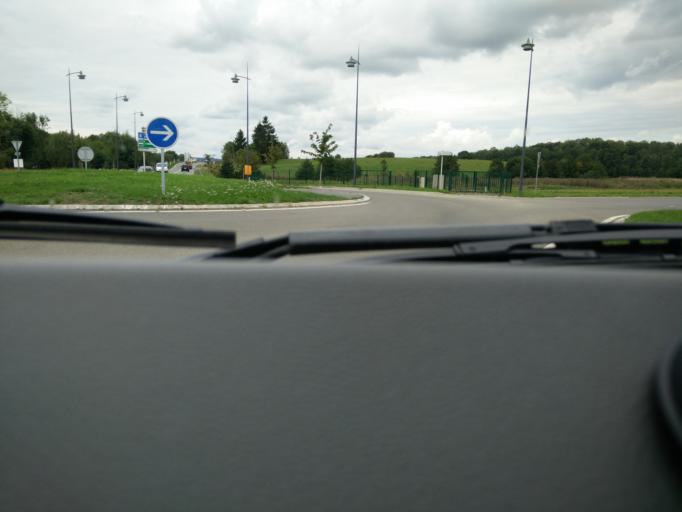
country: FR
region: Champagne-Ardenne
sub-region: Departement des Ardennes
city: Douzy
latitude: 49.6720
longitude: 5.0295
